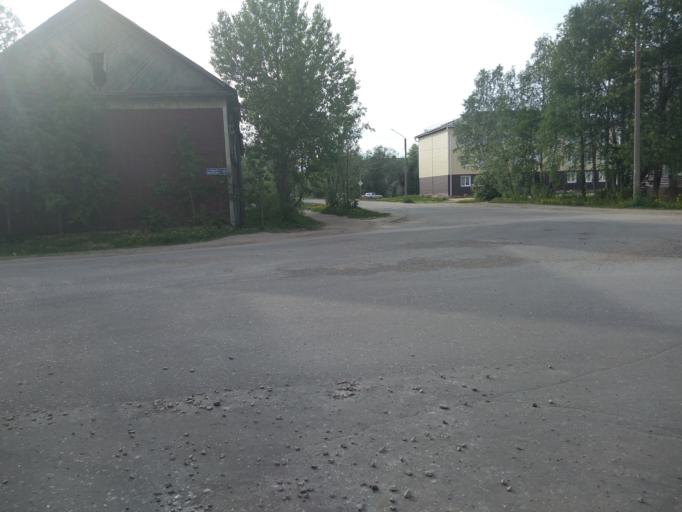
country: RU
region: Komi Republic
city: Pechora
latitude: 65.1449
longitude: 57.2271
